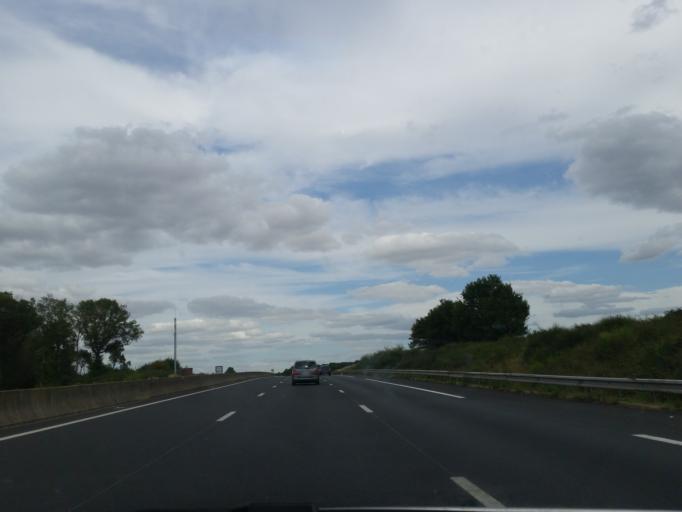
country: FR
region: Centre
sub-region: Departement d'Indre-et-Loire
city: Auzouer-en-Touraine
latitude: 47.5273
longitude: 0.9440
